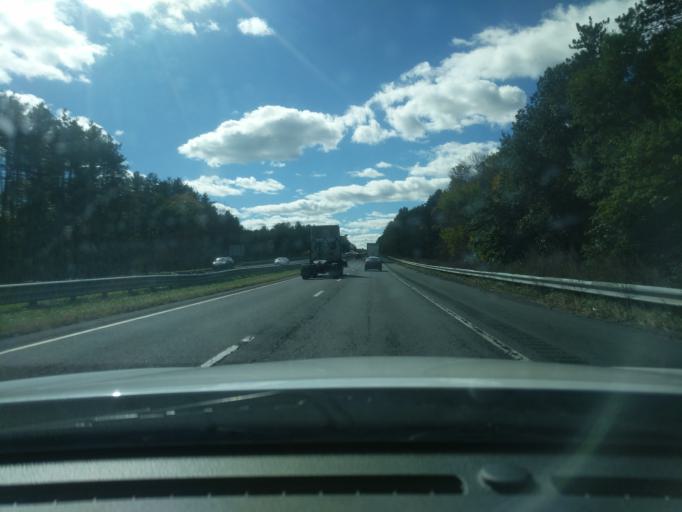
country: US
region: Massachusetts
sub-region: Hampden County
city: Chicopee
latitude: 42.1477
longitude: -72.6730
